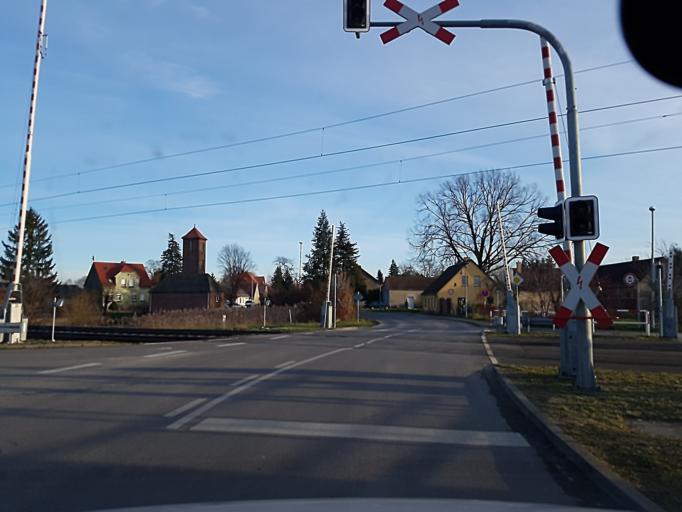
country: DE
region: Brandenburg
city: Finsterwalde
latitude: 51.6443
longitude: 13.7273
